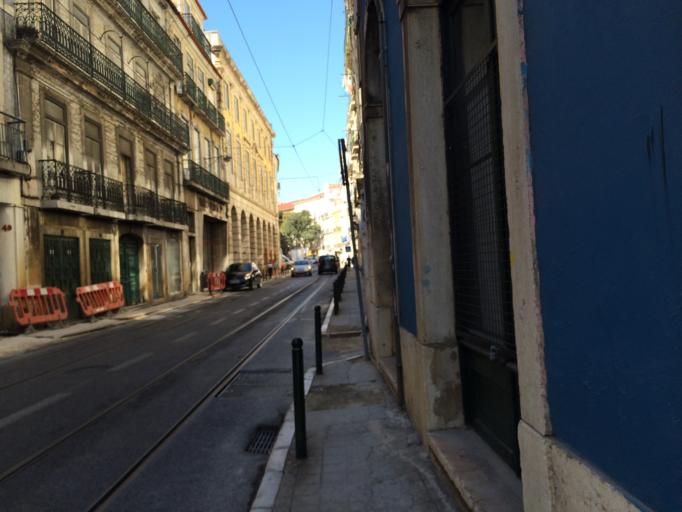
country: PT
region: Lisbon
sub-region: Lisbon
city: Lisbon
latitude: 38.7089
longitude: -9.1491
